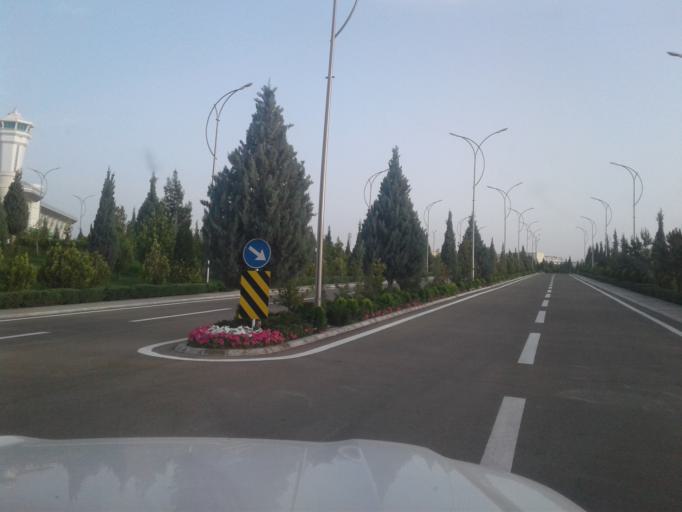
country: TM
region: Balkan
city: Turkmenbasy
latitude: 40.0452
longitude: 52.9927
